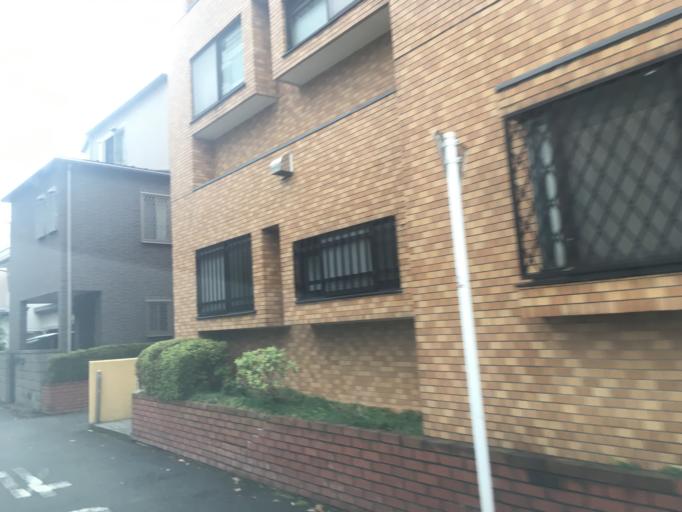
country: JP
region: Tokyo
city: Higashimurayama-shi
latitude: 35.7559
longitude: 139.4632
